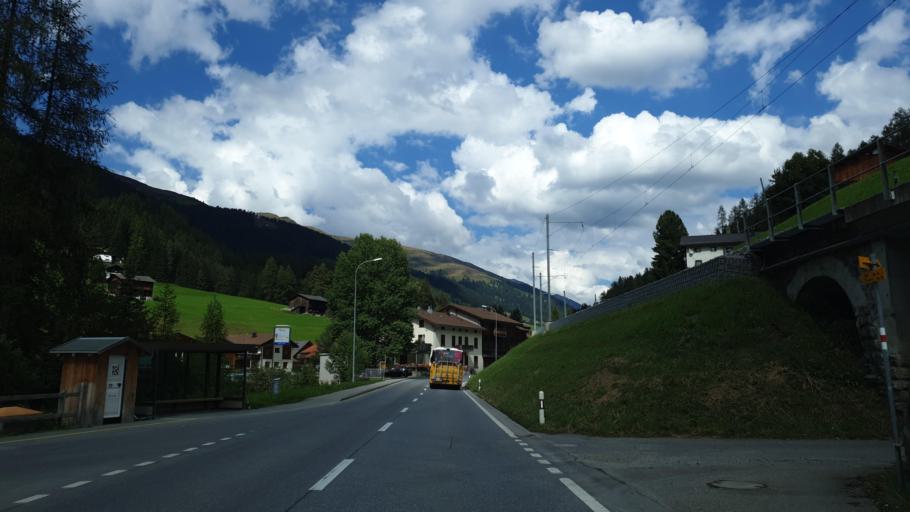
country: CH
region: Grisons
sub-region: Praettigau/Davos District
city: Davos
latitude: 46.7406
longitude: 9.7779
